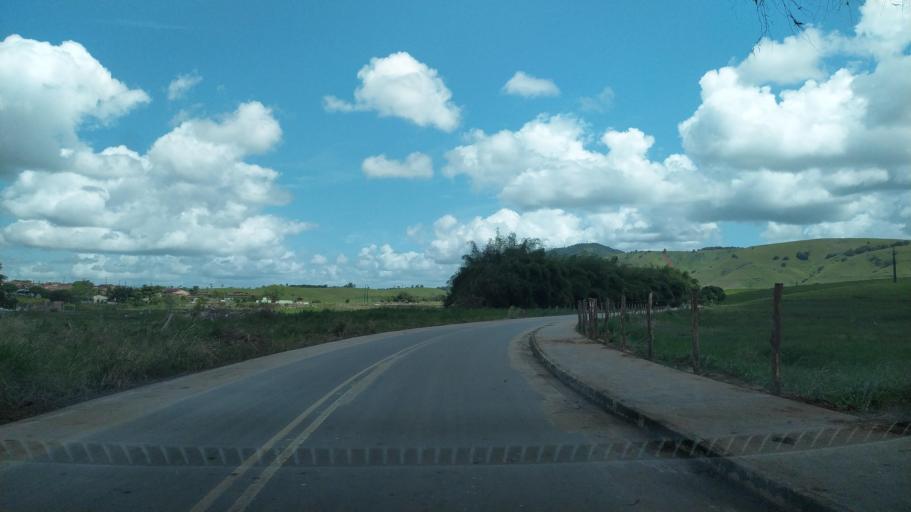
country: BR
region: Alagoas
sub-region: Uniao Dos Palmares
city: Uniao dos Palmares
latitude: -9.1564
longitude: -36.0379
